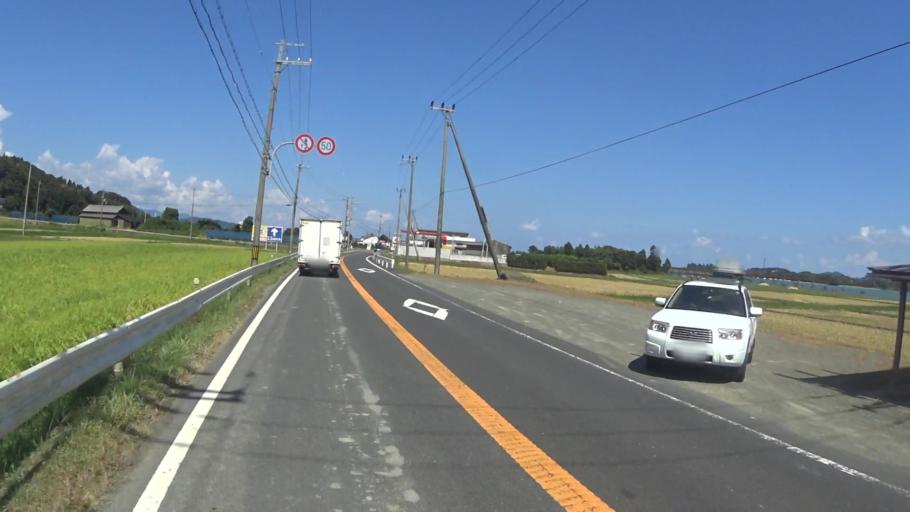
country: JP
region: Kyoto
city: Maizuru
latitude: 35.5049
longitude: 135.2838
